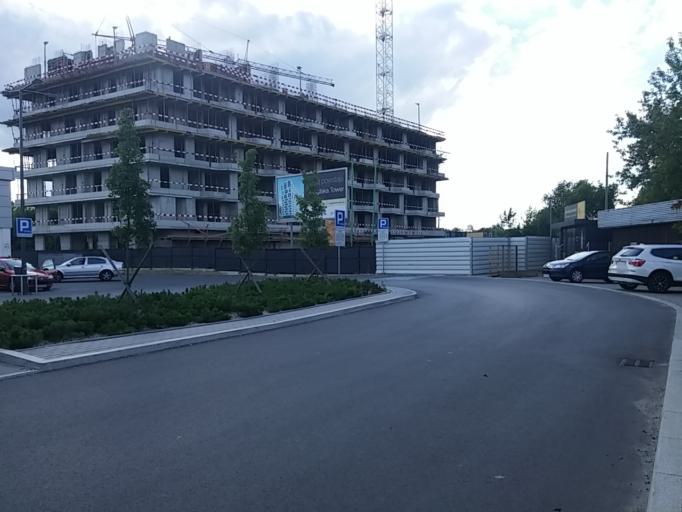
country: PL
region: Lesser Poland Voivodeship
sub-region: Krakow
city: Krakow
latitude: 50.0682
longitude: 19.9775
